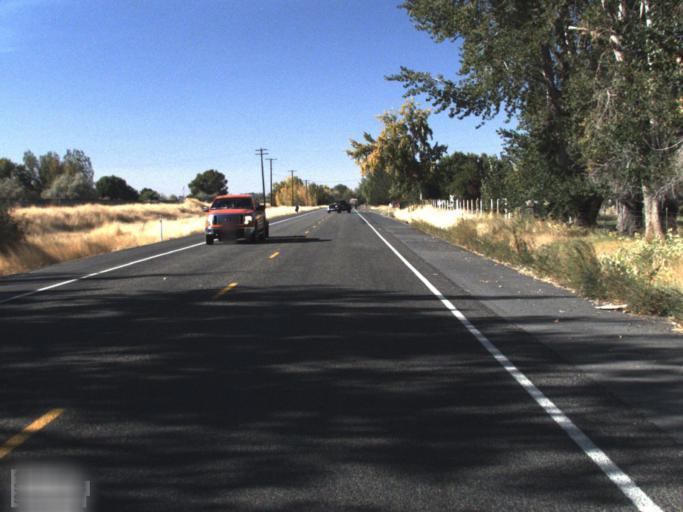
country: US
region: Washington
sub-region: Benton County
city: Finley
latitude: 46.1638
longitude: -119.0440
